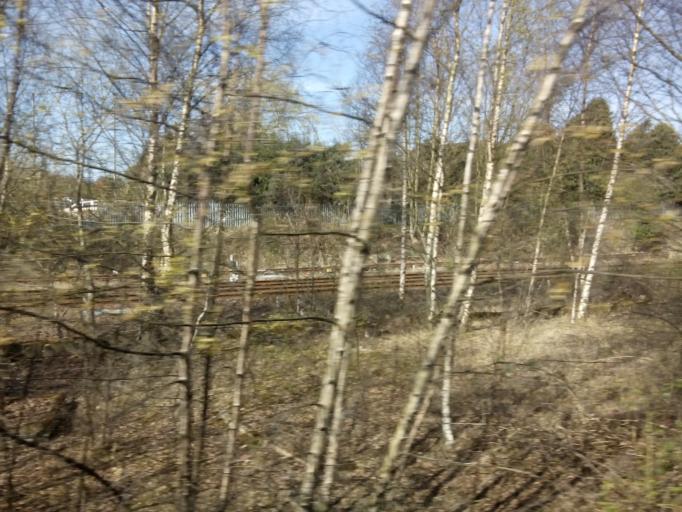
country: GB
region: Scotland
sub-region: Fife
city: Inverkeithing
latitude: 56.0379
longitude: -3.3959
